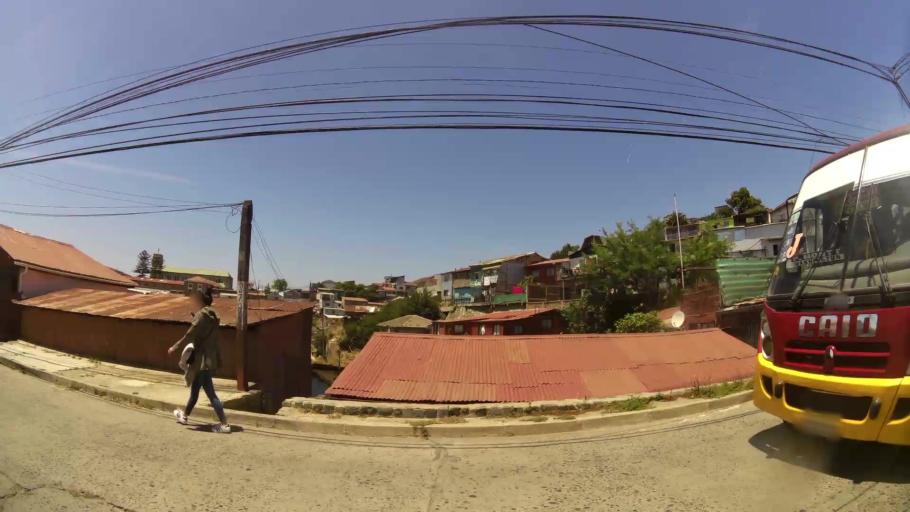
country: CL
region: Valparaiso
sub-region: Provincia de Valparaiso
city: Valparaiso
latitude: -33.0410
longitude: -71.6373
